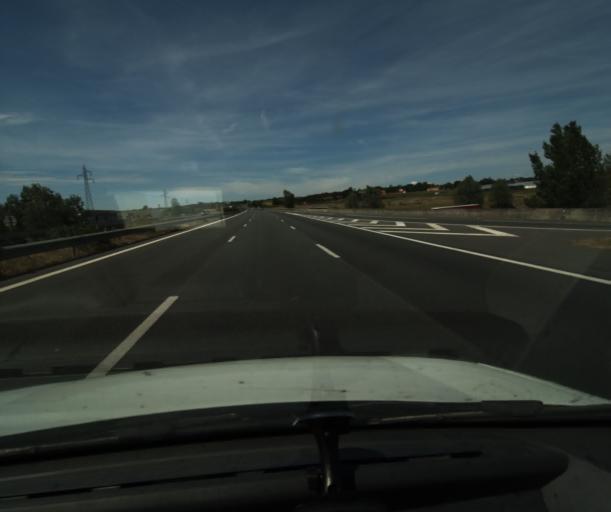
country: FR
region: Midi-Pyrenees
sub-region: Departement de la Haute-Garonne
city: Saint-Sauveur
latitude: 43.7661
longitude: 1.3855
